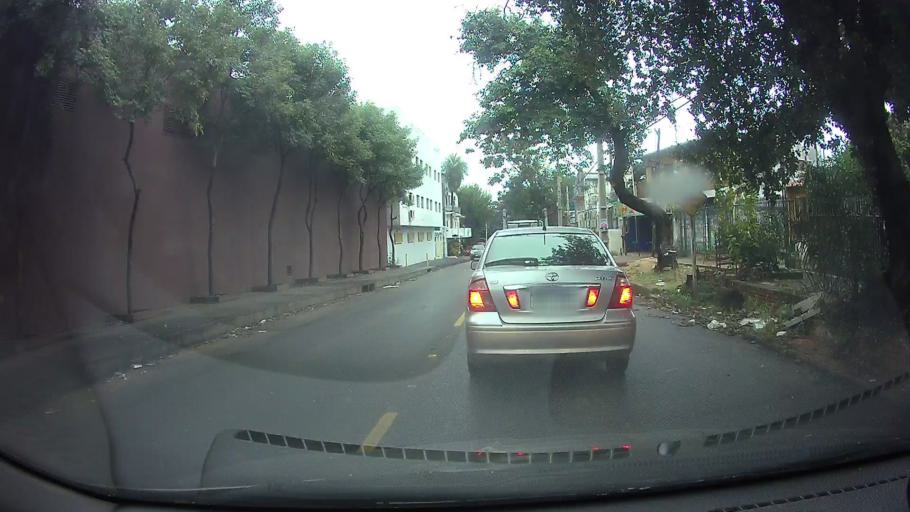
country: PY
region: Central
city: Villa Elisa
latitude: -25.3476
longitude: -57.5724
